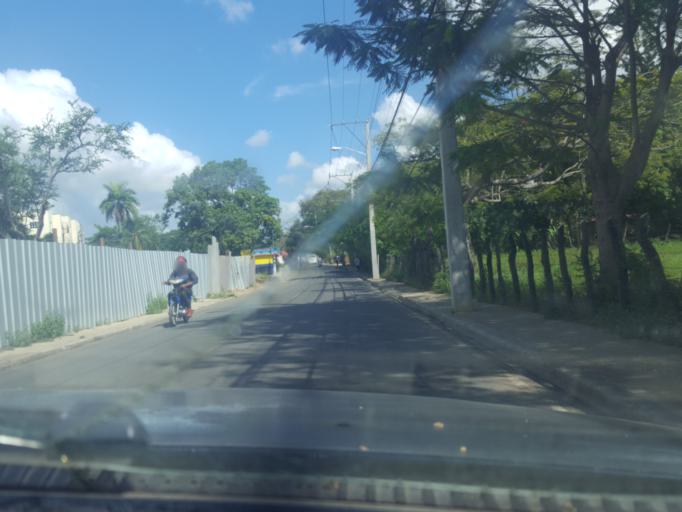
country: DO
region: Santiago
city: Santiago de los Caballeros
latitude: 19.4865
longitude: -70.6995
